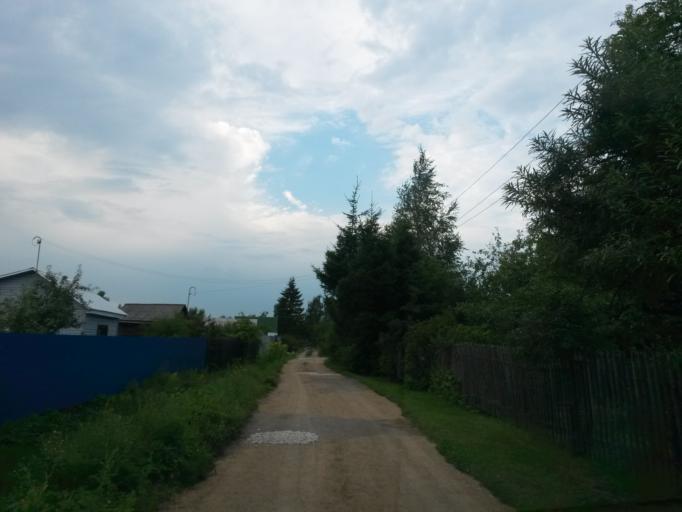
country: RU
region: Jaroslavl
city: Yaroslavl
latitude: 57.6088
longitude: 39.7853
